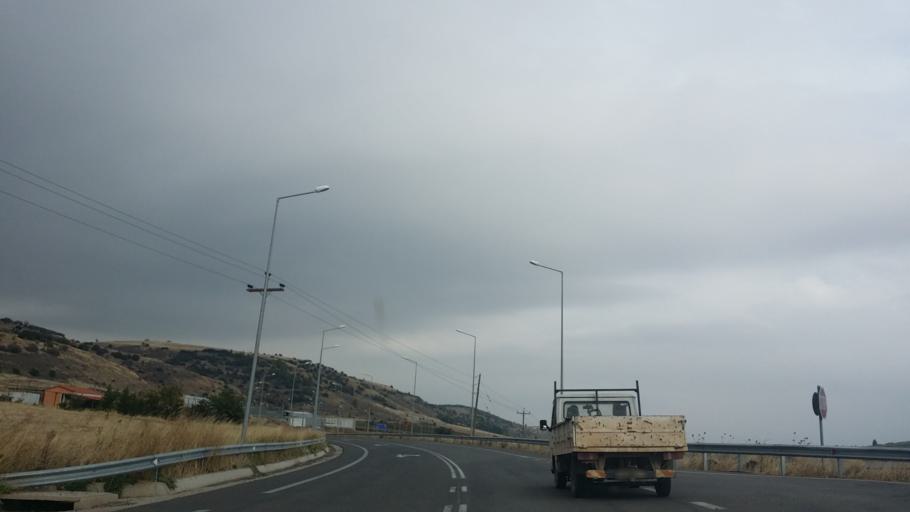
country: GR
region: Central Greece
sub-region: Nomos Voiotias
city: Thespies
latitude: 38.2966
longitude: 23.1666
